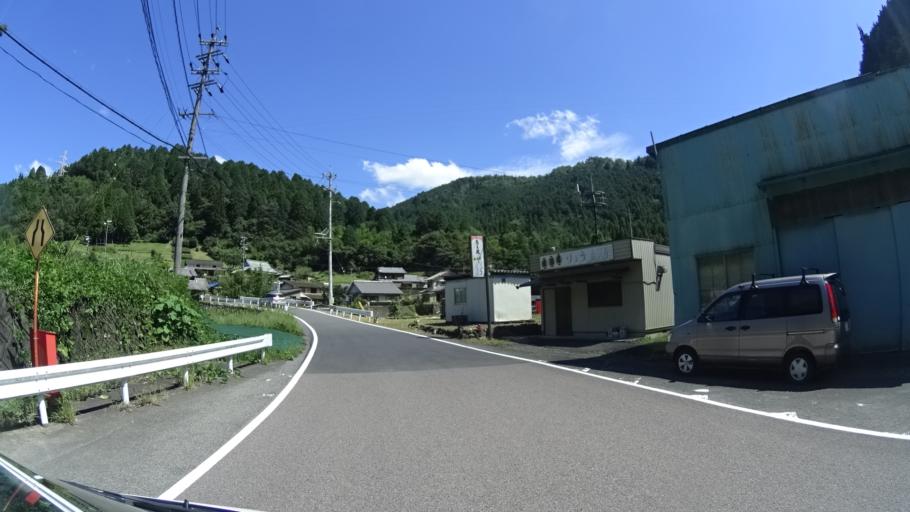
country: JP
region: Gifu
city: Minokamo
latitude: 35.5620
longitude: 137.1088
